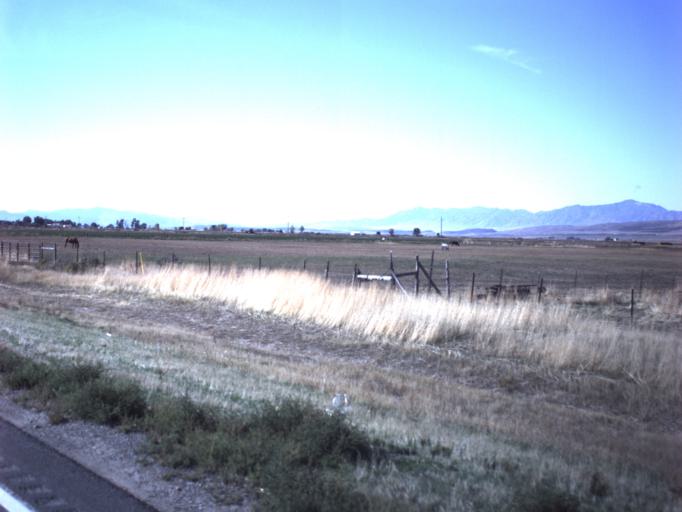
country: US
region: Utah
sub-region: Juab County
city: Nephi
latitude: 39.5758
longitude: -111.8618
